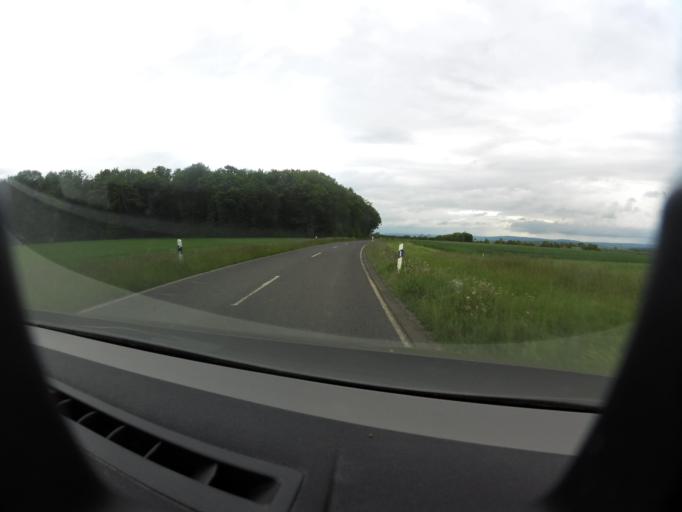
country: DE
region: Bavaria
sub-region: Regierungsbezirk Unterfranken
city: Nordheim
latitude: 49.8856
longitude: 10.2025
